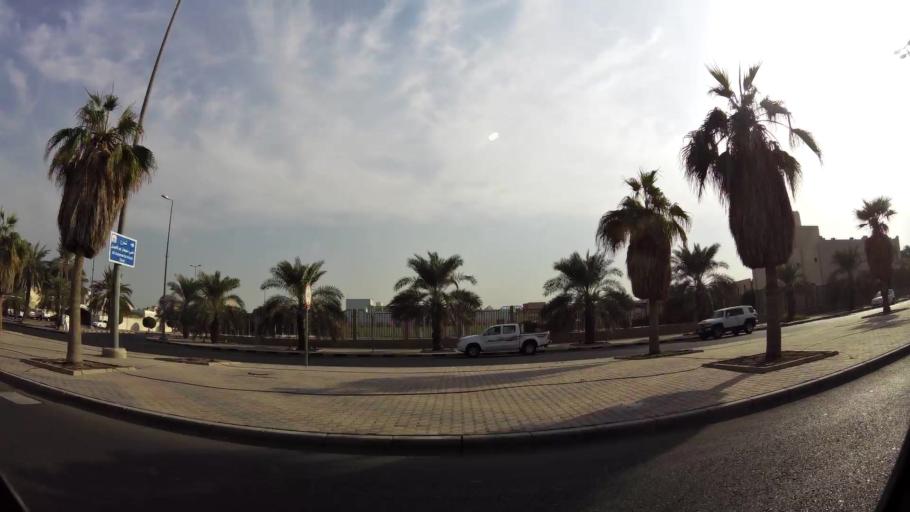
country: KW
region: Muhafazat Hawalli
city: Hawalli
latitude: 29.3299
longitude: 47.9966
